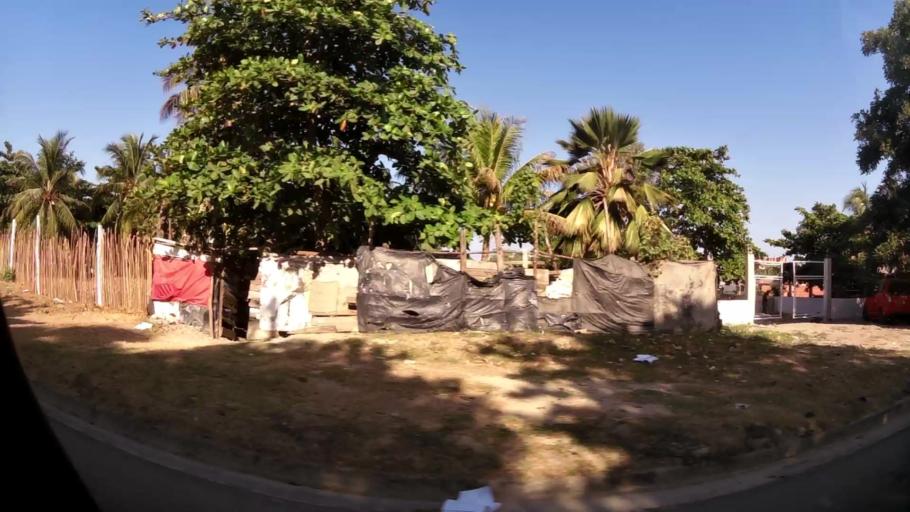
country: CO
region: Bolivar
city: Cartagena
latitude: 10.4734
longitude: -75.4945
